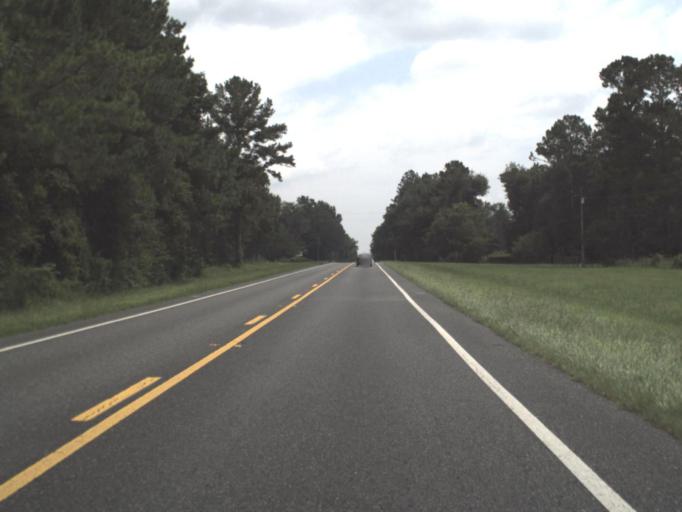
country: US
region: Florida
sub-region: Alachua County
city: High Springs
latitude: 29.9687
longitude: -82.6016
